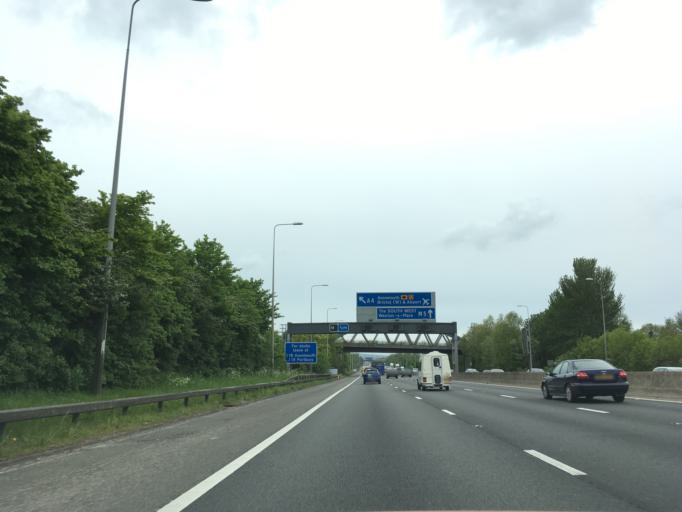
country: GB
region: England
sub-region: South Gloucestershire
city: Severn Beach
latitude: 51.5143
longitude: -2.6491
